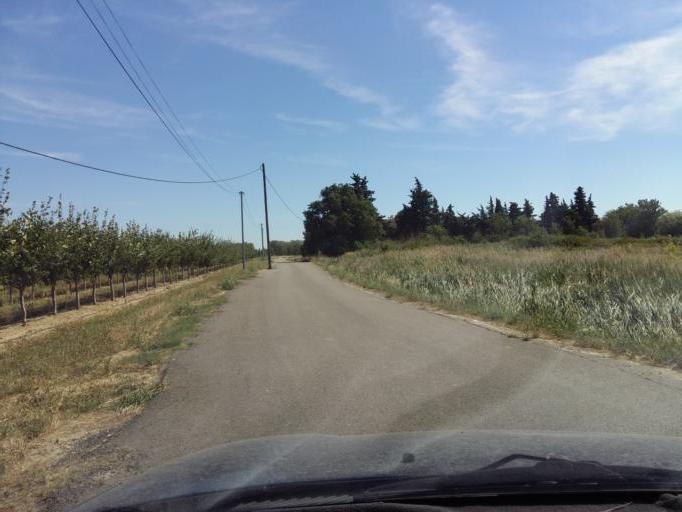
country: FR
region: Provence-Alpes-Cote d'Azur
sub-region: Departement du Vaucluse
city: Piolenc
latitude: 44.1754
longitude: 4.7502
